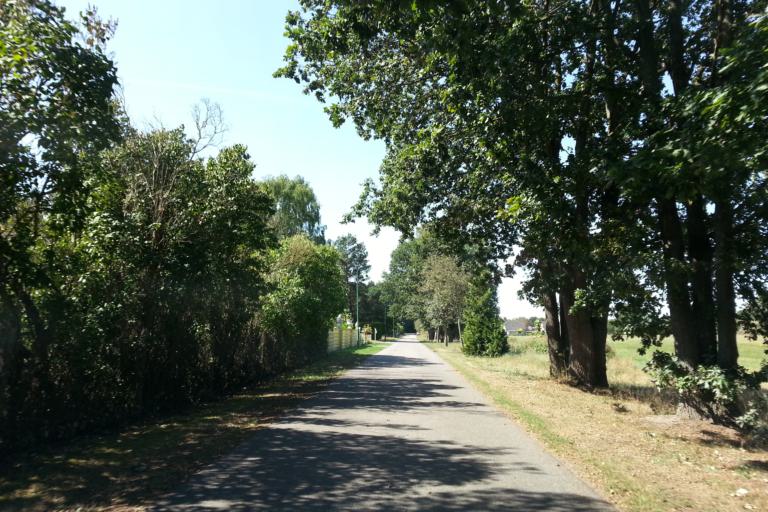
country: DE
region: Mecklenburg-Vorpommern
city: Ferdinandshof
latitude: 53.6406
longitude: 13.9301
